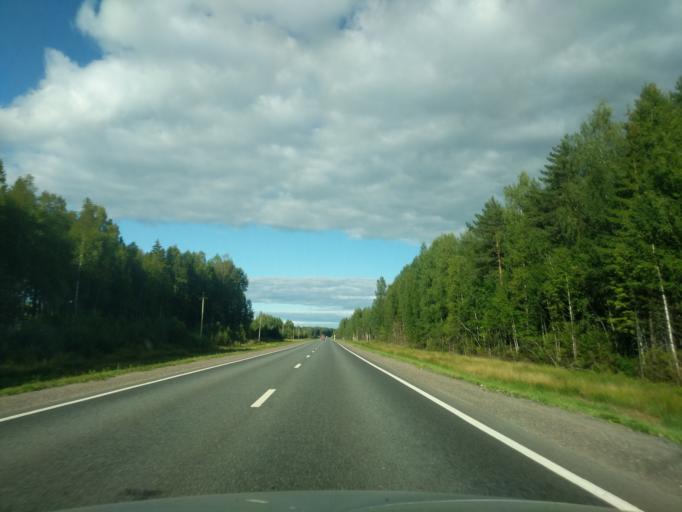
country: RU
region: Kostroma
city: Manturovo
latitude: 58.1575
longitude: 44.3871
